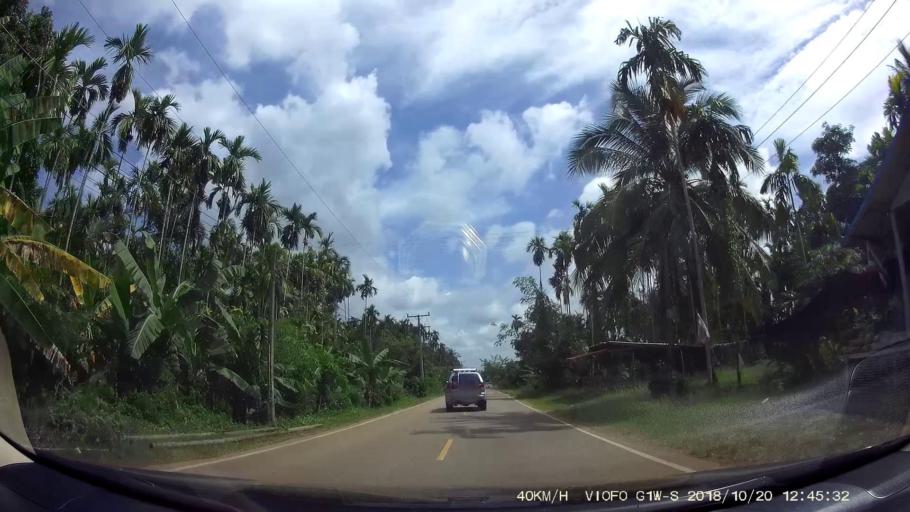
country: TH
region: Chaiyaphum
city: Khon San
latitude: 16.5362
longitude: 101.8745
